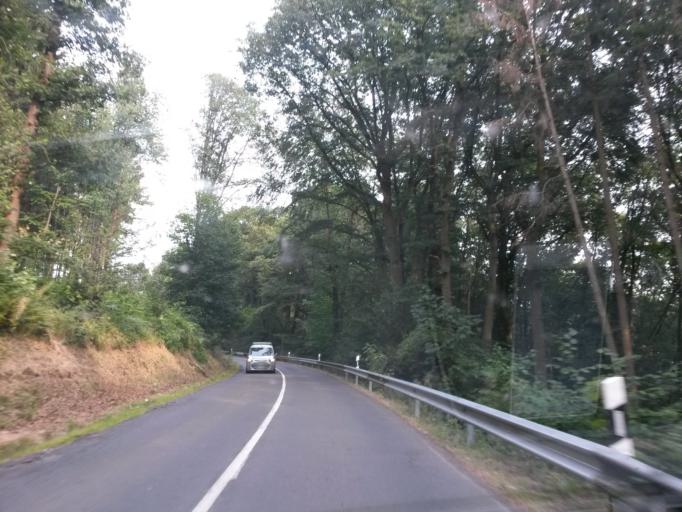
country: DE
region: North Rhine-Westphalia
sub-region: Regierungsbezirk Koln
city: Hennef
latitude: 50.7852
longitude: 7.2960
